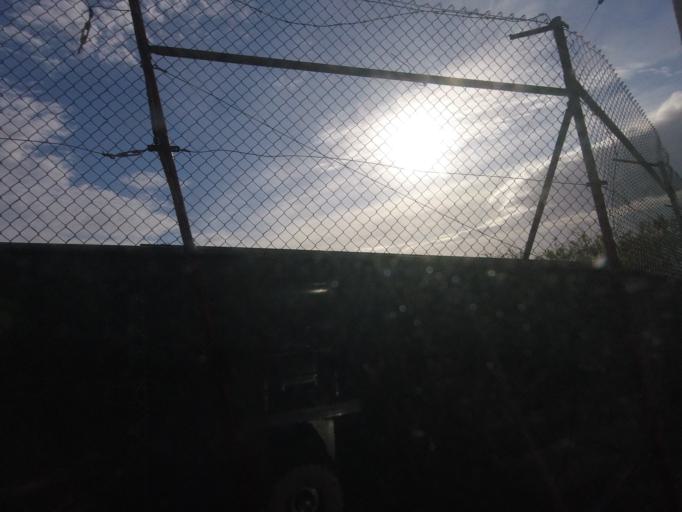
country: PT
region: Madeira
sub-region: Machico
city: Canical
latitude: 32.7448
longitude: -16.7385
